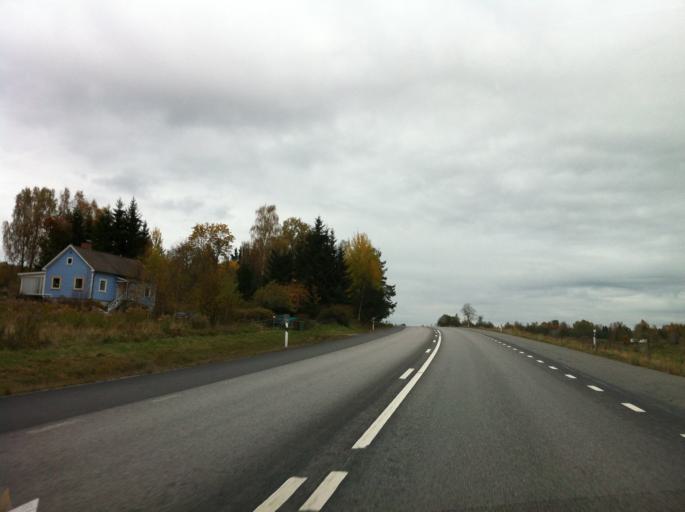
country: SE
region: OErebro
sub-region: Lindesbergs Kommun
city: Stora
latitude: 59.7254
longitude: 15.1337
